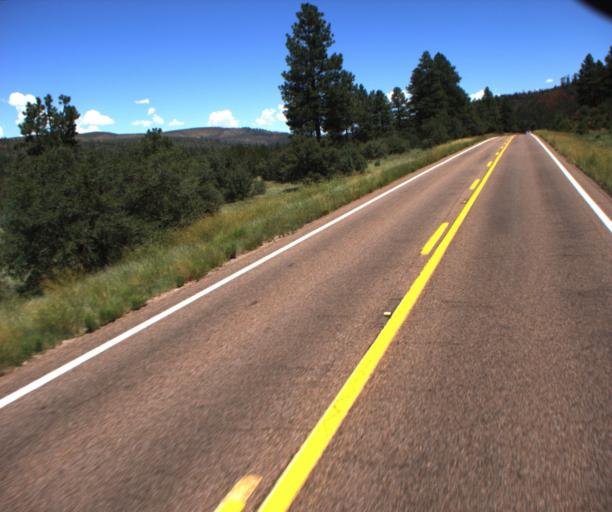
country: US
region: Arizona
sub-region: Navajo County
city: Linden
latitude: 34.0659
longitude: -110.2006
